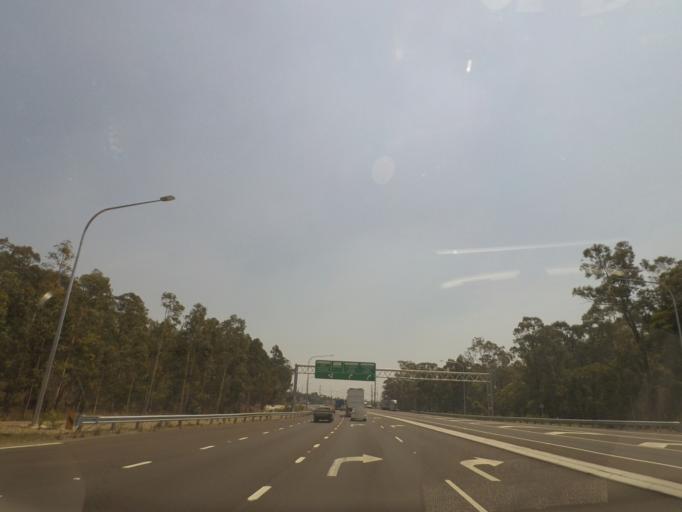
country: AU
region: New South Wales
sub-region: Newcastle
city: Beresfield
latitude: -32.8165
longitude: 151.6356
